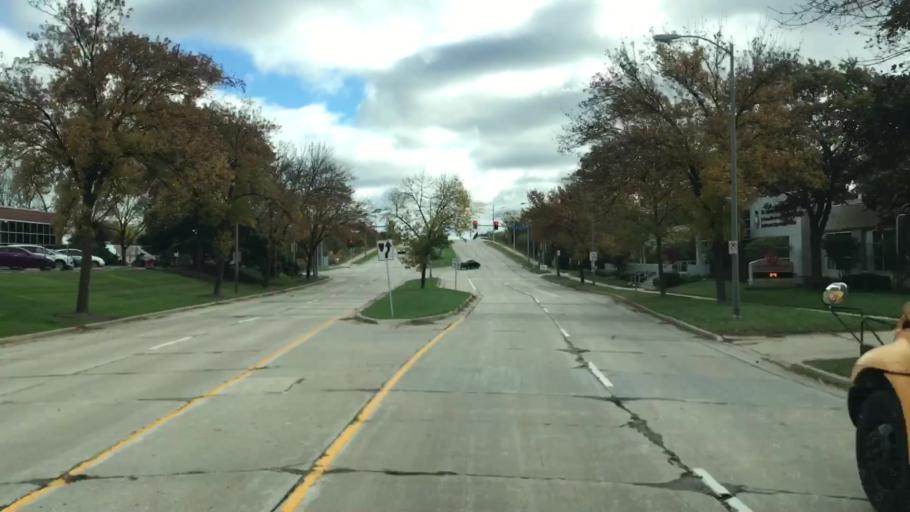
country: US
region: Wisconsin
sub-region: Waukesha County
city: Elm Grove
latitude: 43.0455
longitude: -88.0555
